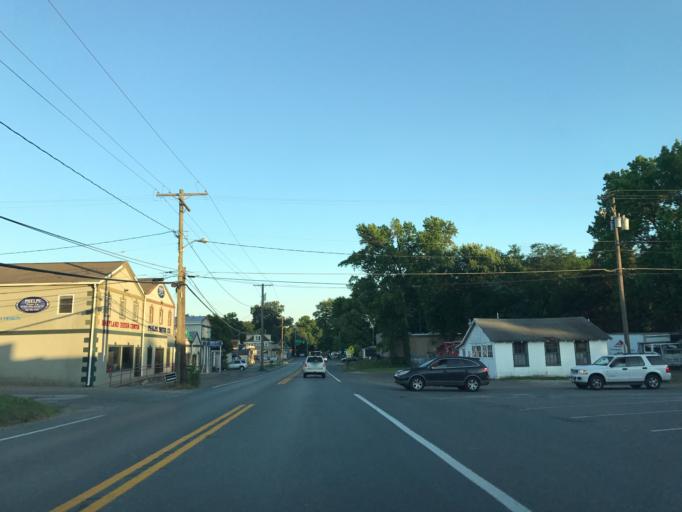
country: US
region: Maryland
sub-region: Anne Arundel County
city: Londontowne
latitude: 38.9325
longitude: -76.5571
